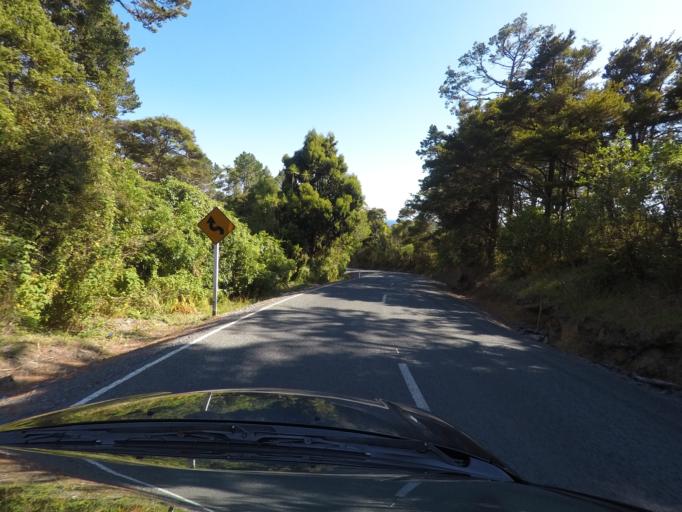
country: NZ
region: Auckland
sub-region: Auckland
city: Warkworth
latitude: -36.2801
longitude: 174.7916
